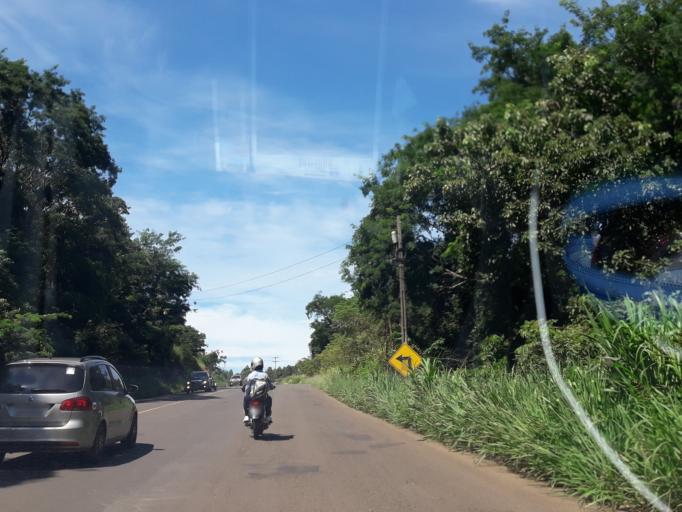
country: AR
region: Misiones
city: Bernardo de Irigoyen
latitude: -26.5820
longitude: -53.5173
